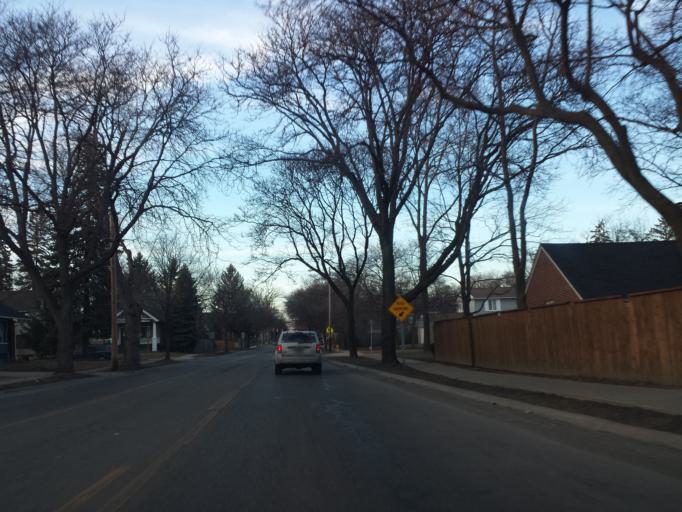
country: US
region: Michigan
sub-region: Oakland County
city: Birmingham
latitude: 42.5474
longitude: -83.2058
